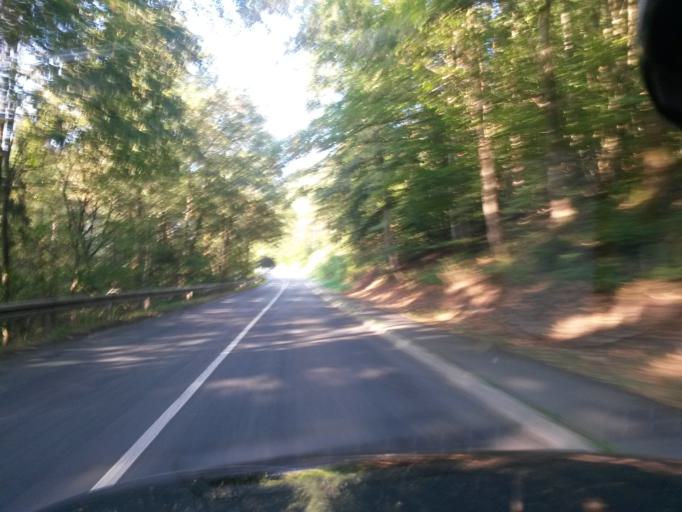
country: DE
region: North Rhine-Westphalia
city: Bergneustadt
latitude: 51.0316
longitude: 7.6280
